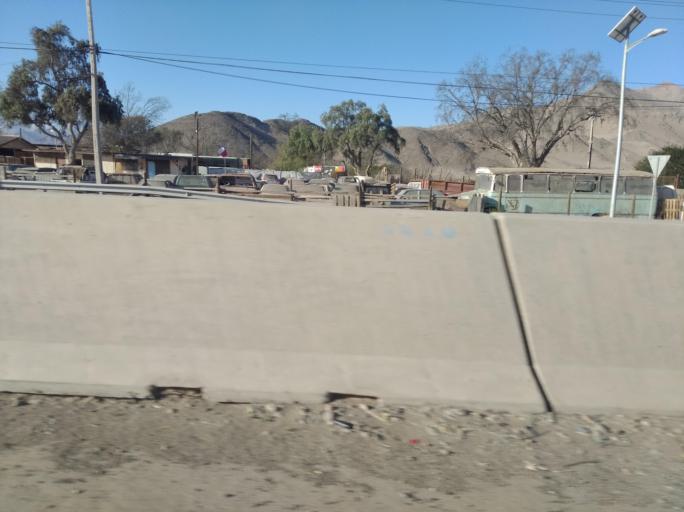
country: CL
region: Atacama
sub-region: Provincia de Copiapo
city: Copiapo
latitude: -27.3389
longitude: -70.3749
